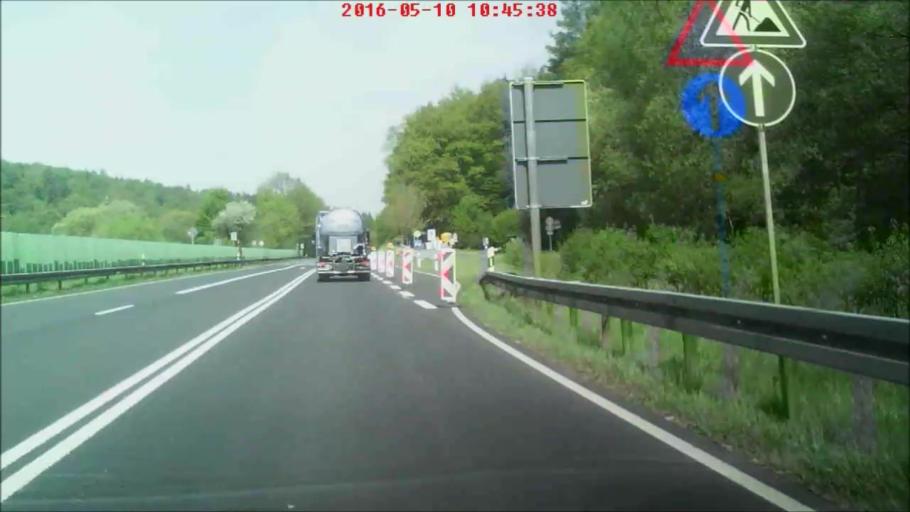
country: DE
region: Hesse
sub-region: Regierungsbezirk Kassel
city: Burghaun
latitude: 50.7338
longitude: 9.6960
